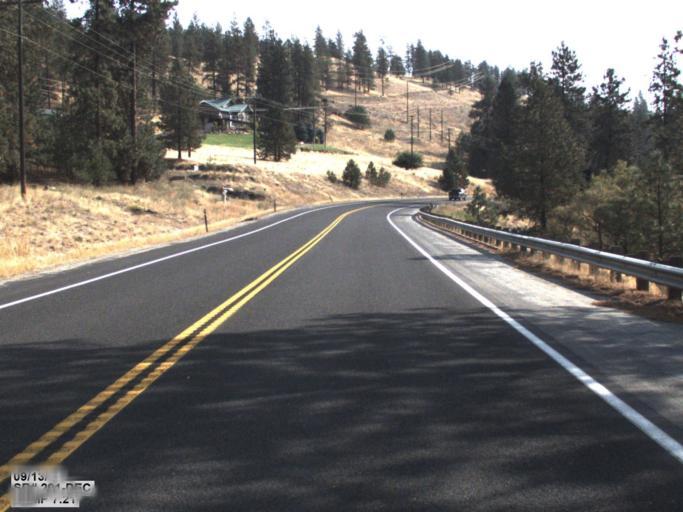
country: US
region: Washington
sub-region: Spokane County
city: Fairwood
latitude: 47.7591
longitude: -117.5267
